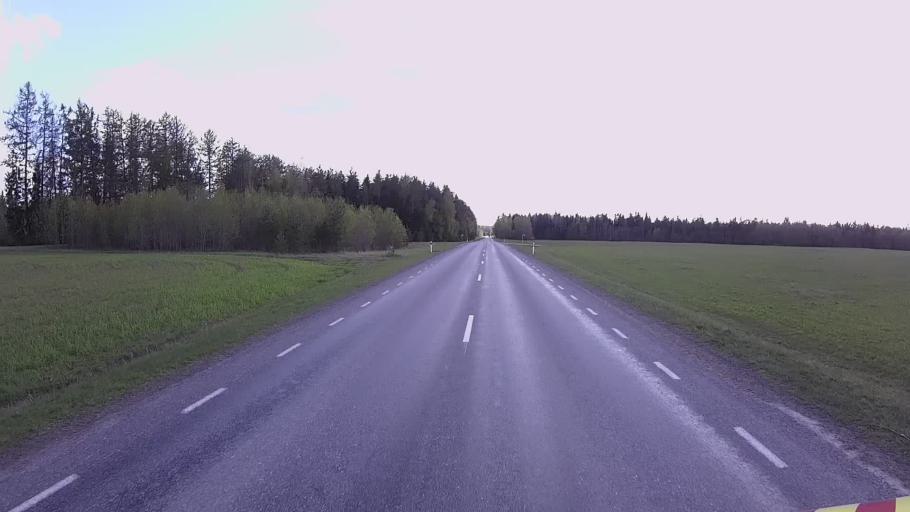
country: EE
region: Jogevamaa
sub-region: Jogeva linn
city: Jogeva
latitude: 58.7482
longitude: 26.3111
